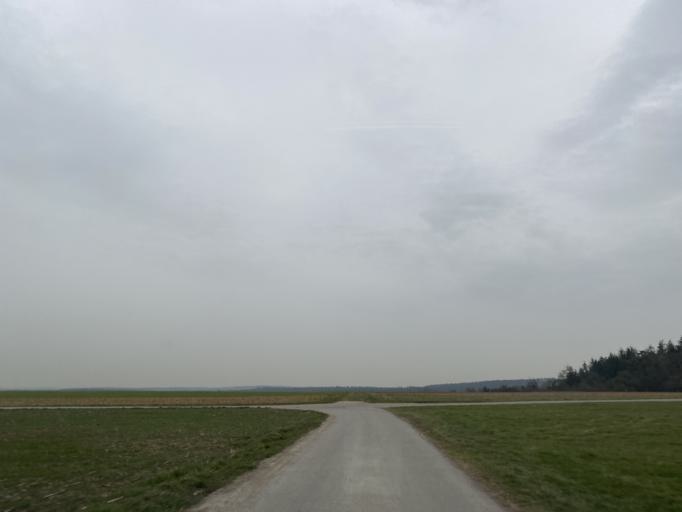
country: DE
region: Baden-Wuerttemberg
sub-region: Regierungsbezirk Stuttgart
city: Eberdingen
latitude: 48.8850
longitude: 8.9315
